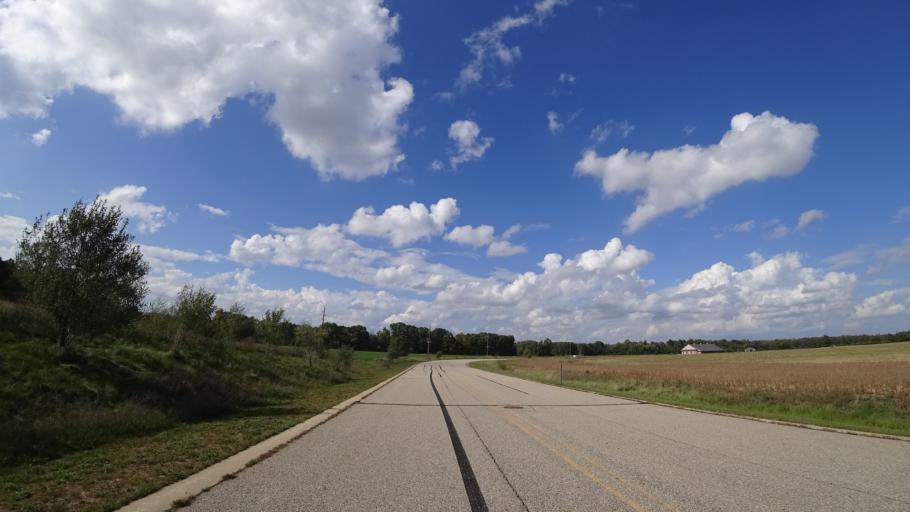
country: US
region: Michigan
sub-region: Saint Joseph County
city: Three Rivers
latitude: 41.9585
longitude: -85.6125
